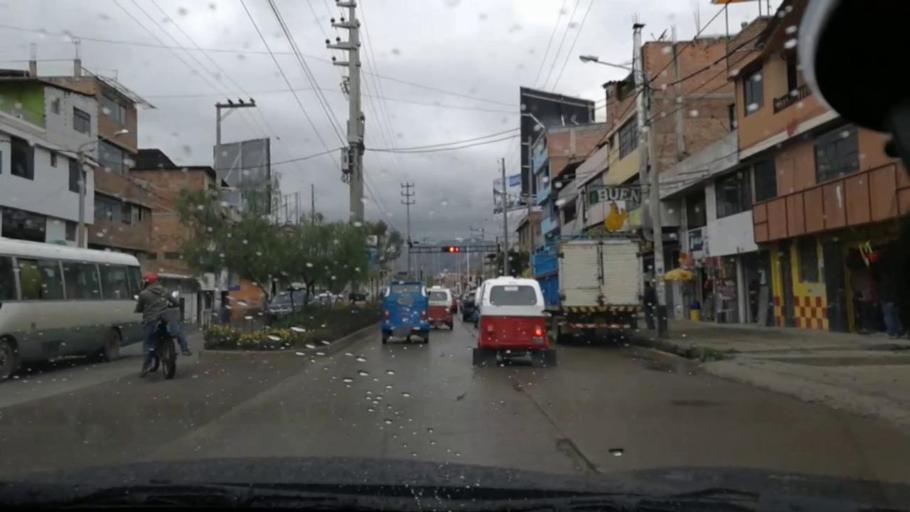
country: PE
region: Cajamarca
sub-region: Provincia de Cajamarca
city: Cajamarca
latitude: -7.1646
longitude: -78.5032
